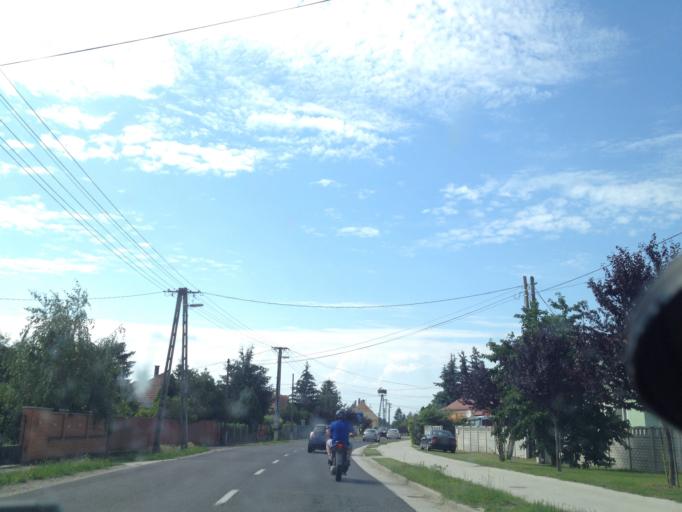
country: HU
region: Veszprem
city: Papa
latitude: 47.2862
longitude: 17.5173
